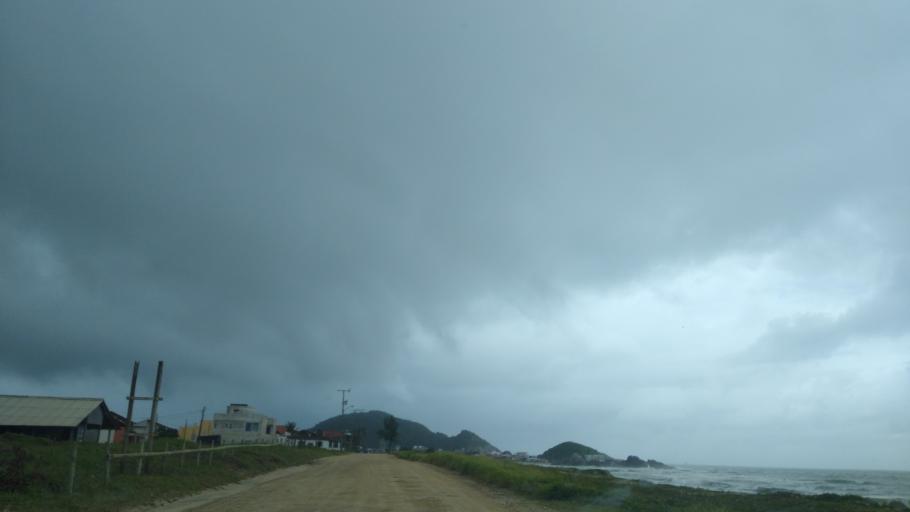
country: BR
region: Santa Catarina
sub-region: Sao Francisco Do Sul
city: Sao Francisco do Sul
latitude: -26.2412
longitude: -48.5073
